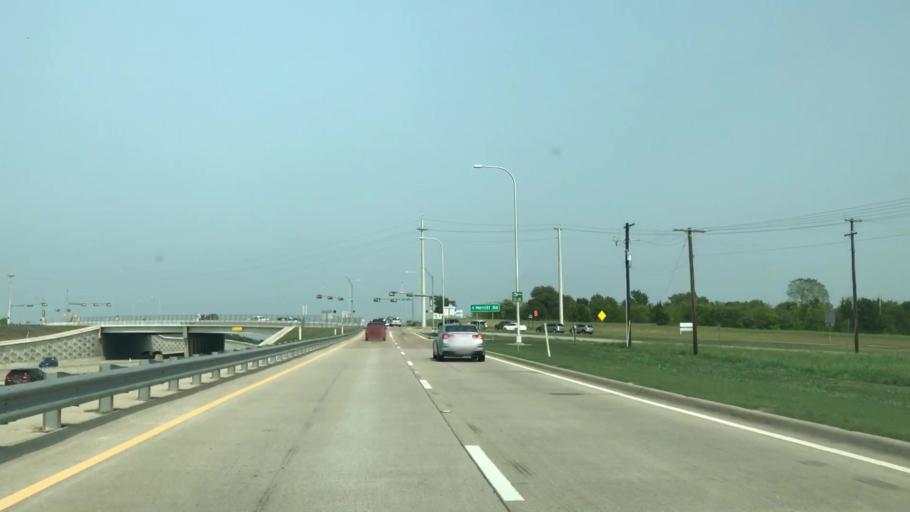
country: US
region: Texas
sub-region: Dallas County
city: Sachse
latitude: 32.9501
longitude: -96.5863
